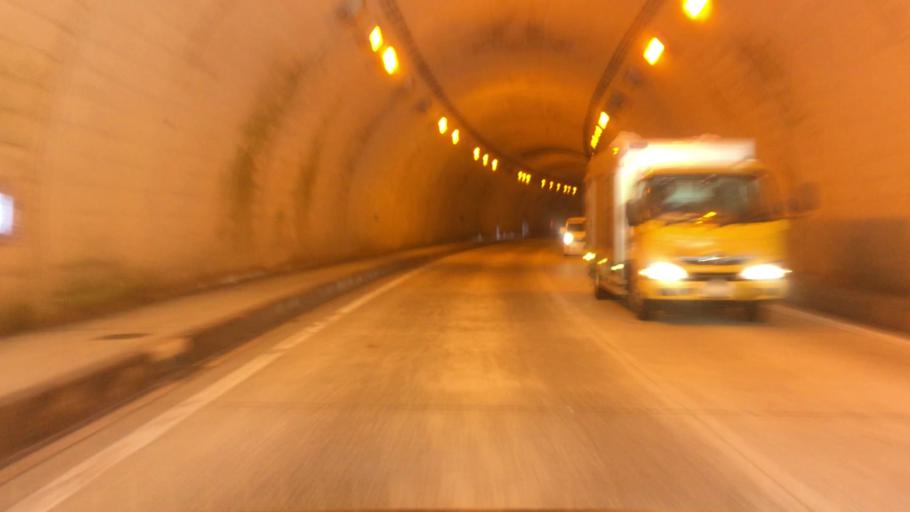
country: JP
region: Tottori
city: Tottori
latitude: 35.6170
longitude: 134.4146
